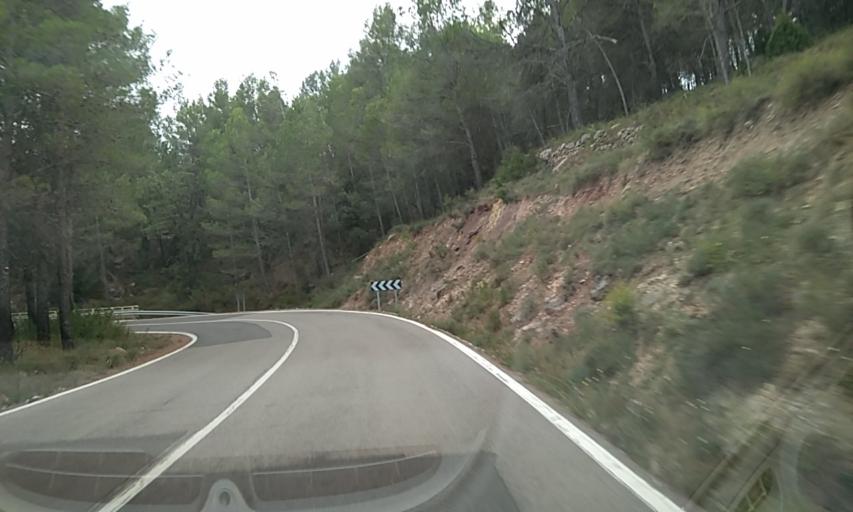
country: ES
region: Valencia
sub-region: Provincia de Castello
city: Puebla de Arenoso
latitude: 40.0925
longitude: -0.5672
